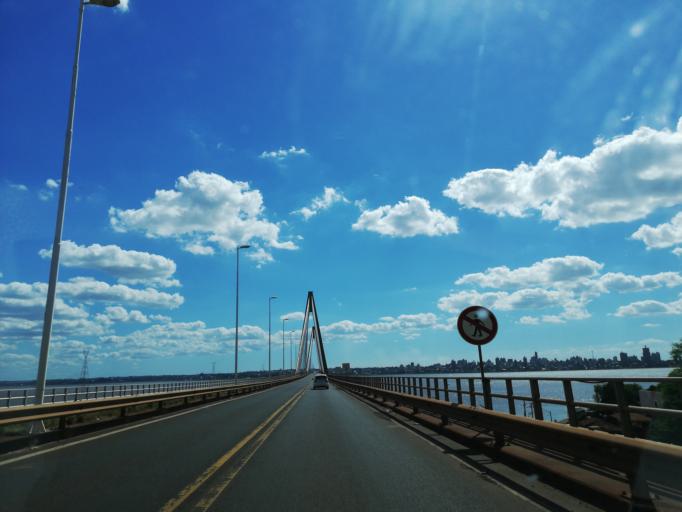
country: PY
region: Itapua
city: Encarnacion
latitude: -27.3671
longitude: -55.8566
